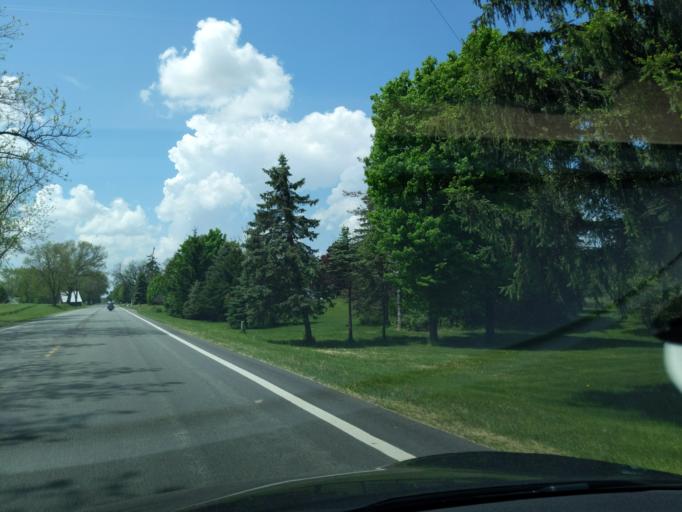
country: US
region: Michigan
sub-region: Ingham County
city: Stockbridge
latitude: 42.5069
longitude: -84.1509
